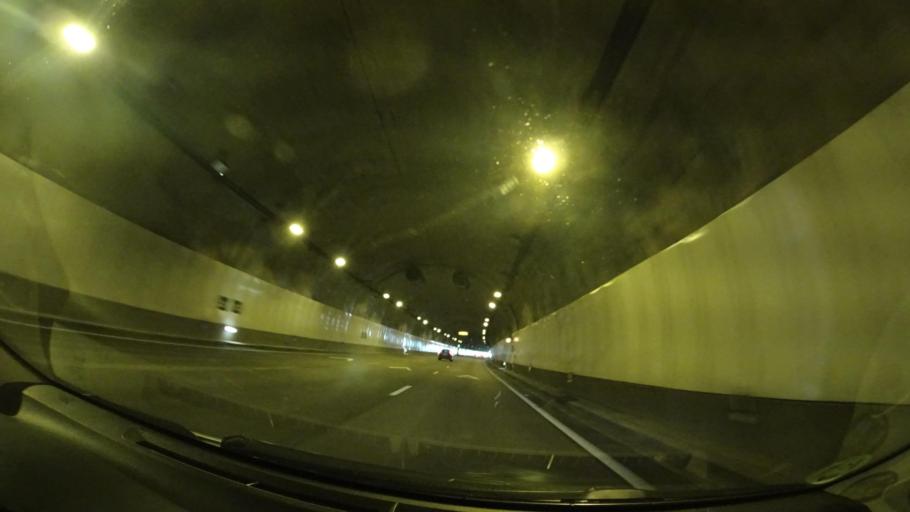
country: ES
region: Andalusia
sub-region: Provincia de Sevilla
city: El Ronquillo
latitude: 37.6478
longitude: -6.1587
